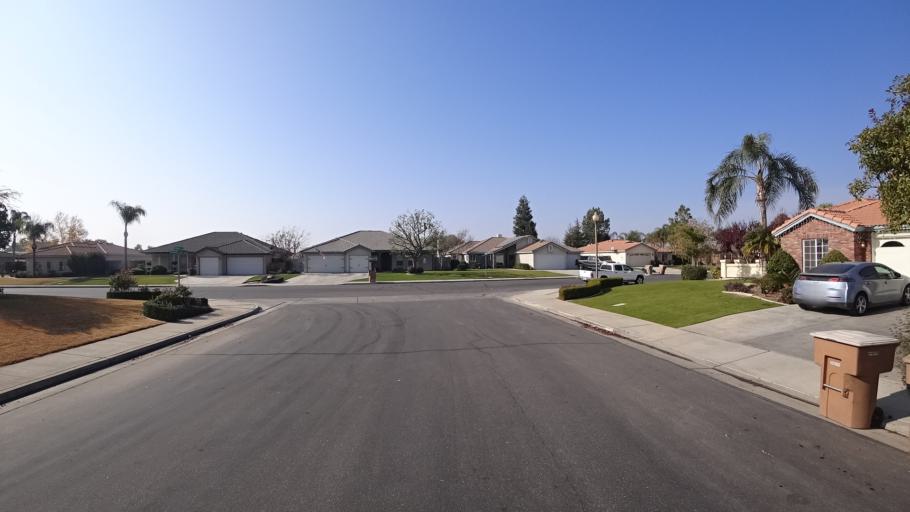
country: US
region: California
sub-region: Kern County
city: Greenacres
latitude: 35.4157
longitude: -119.1116
